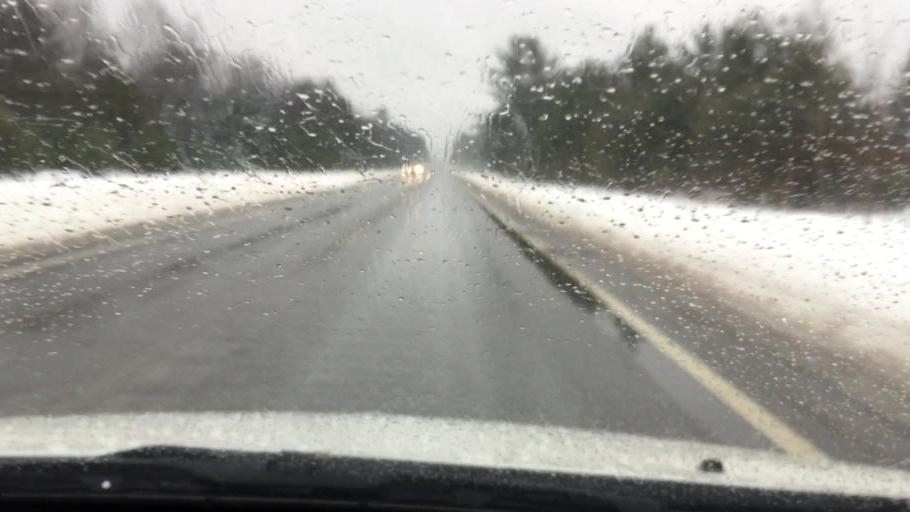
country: US
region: Michigan
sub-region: Charlevoix County
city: East Jordan
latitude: 45.0376
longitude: -85.0680
